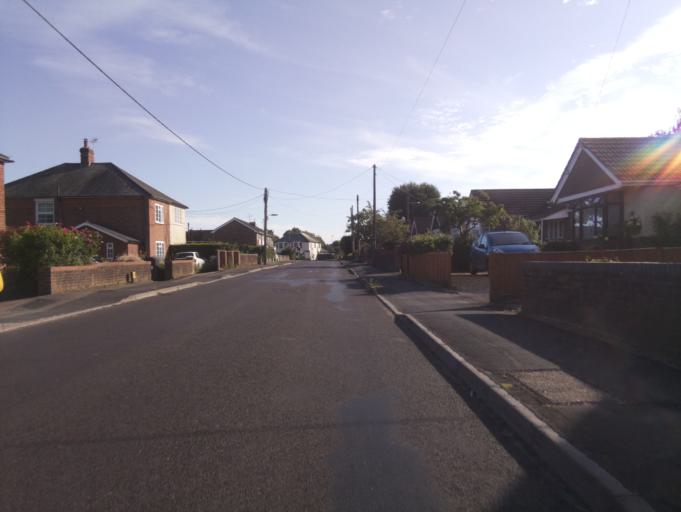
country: GB
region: England
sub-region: Hampshire
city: Chandlers Ford
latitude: 50.9790
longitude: -1.4364
